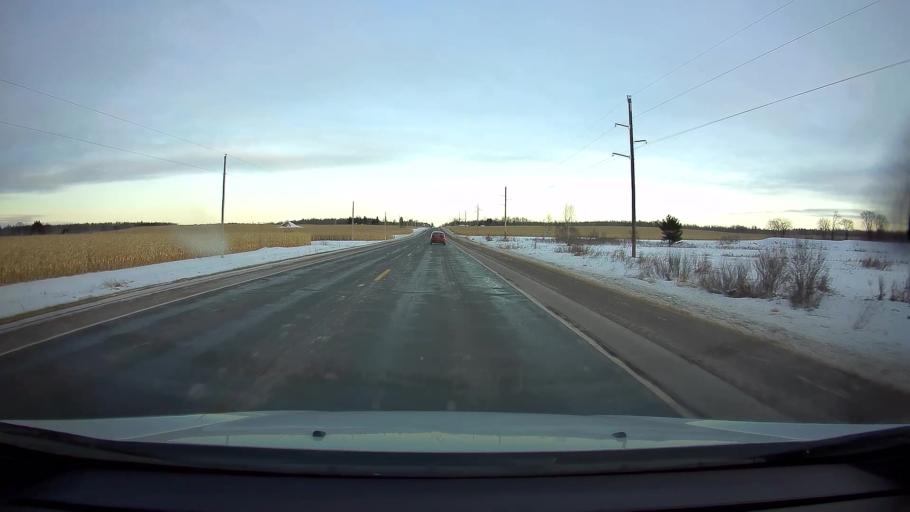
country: US
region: Wisconsin
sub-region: Barron County
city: Turtle Lake
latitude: 45.3457
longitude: -92.1673
